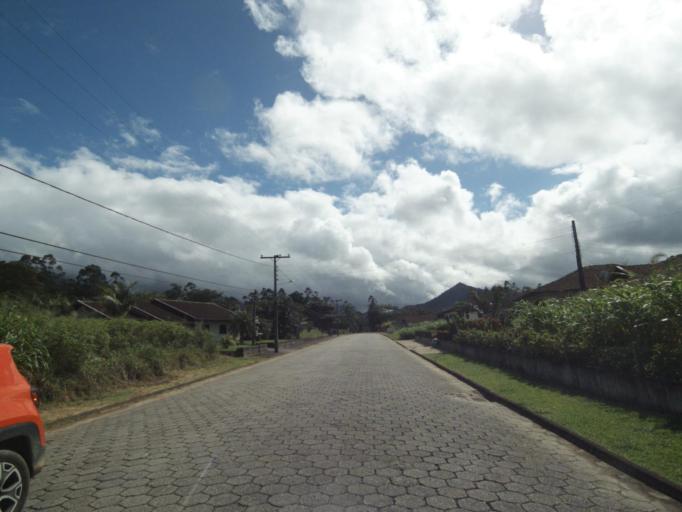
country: BR
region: Santa Catarina
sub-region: Pomerode
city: Pomerode
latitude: -26.6905
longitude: -49.1740
